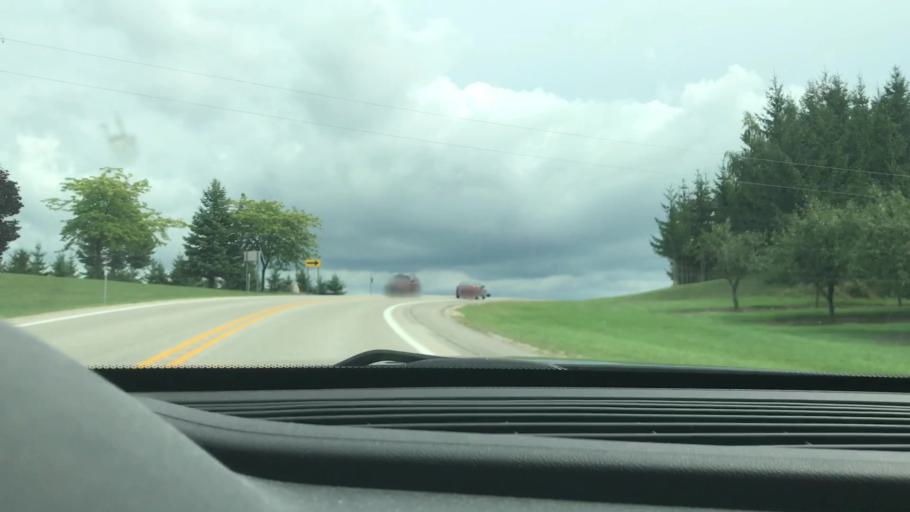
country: US
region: Michigan
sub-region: Antrim County
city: Bellaire
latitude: 45.0987
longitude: -85.3031
